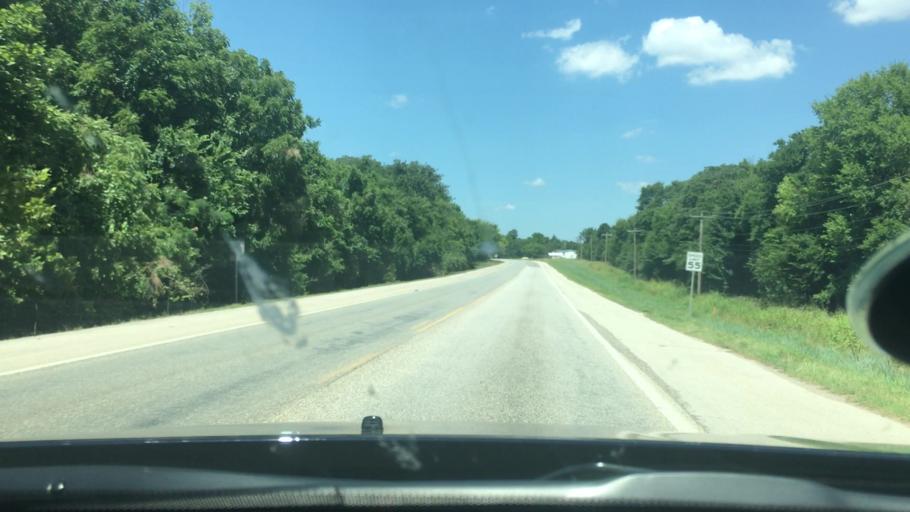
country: US
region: Oklahoma
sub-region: Marshall County
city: Oakland
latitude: 34.1829
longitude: -96.8693
